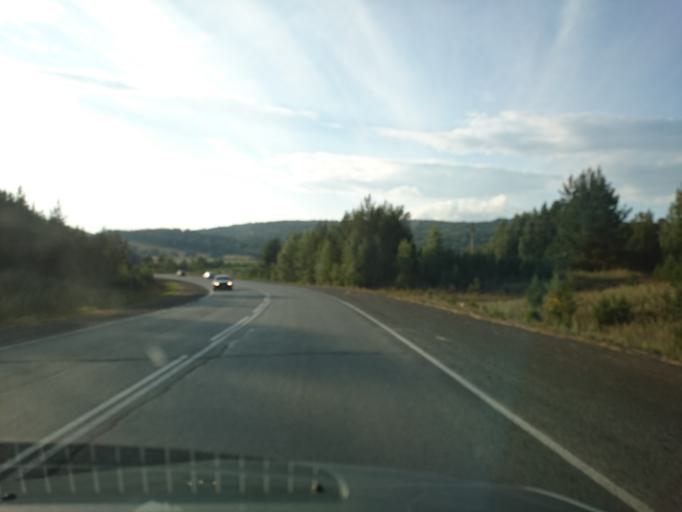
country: RU
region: Bashkortostan
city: Lomovka
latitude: 53.8953
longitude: 58.0916
